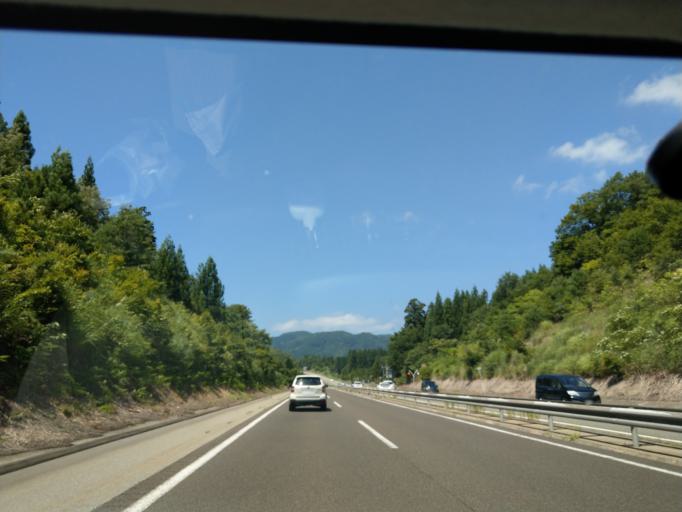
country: JP
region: Akita
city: Omagari
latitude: 39.4162
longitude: 140.4368
